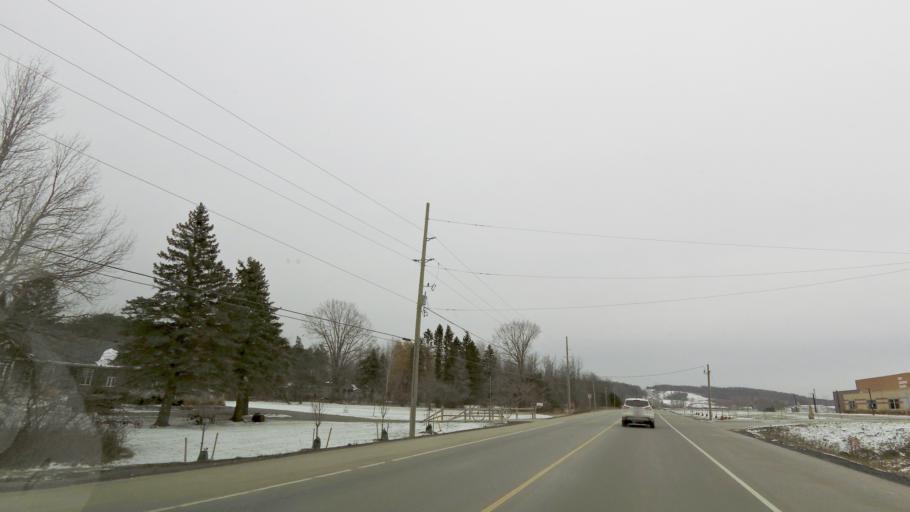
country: CA
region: Ontario
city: Newmarket
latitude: 44.1023
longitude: -79.5196
